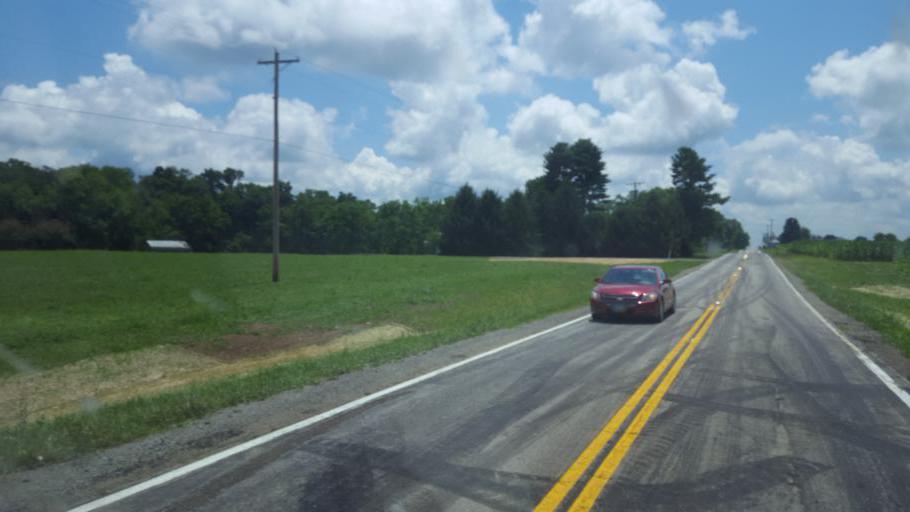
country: US
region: Ohio
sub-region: Highland County
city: Greenfield
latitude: 39.2405
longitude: -83.4318
